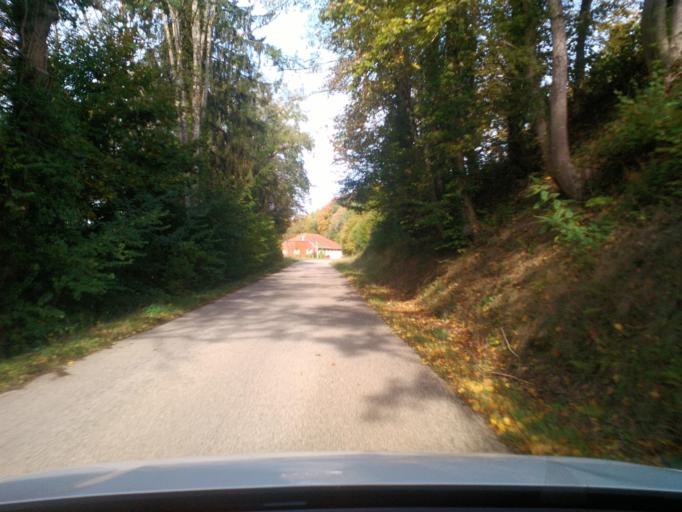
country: FR
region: Lorraine
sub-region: Departement des Vosges
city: Senones
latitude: 48.3629
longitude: 7.0329
